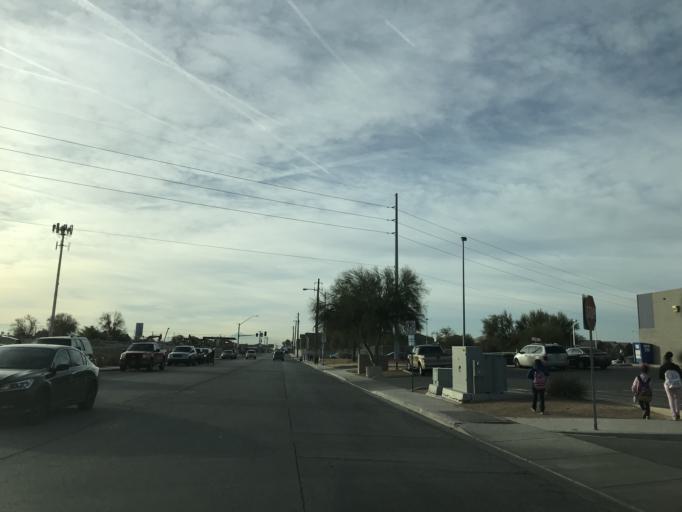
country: US
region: Nevada
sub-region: Clark County
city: Nellis Air Force Base
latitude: 36.2378
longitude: -115.0667
